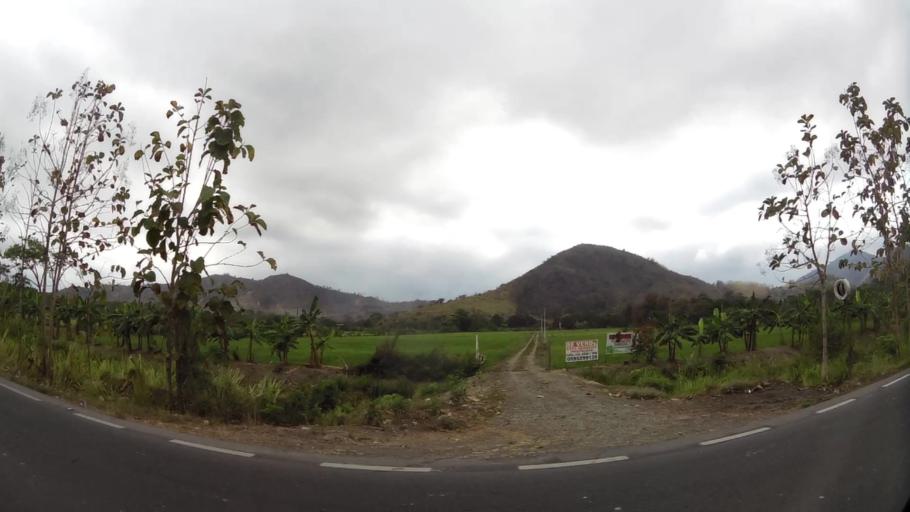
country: EC
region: Guayas
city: Coronel Marcelino Mariduena
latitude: -2.3896
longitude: -79.6306
